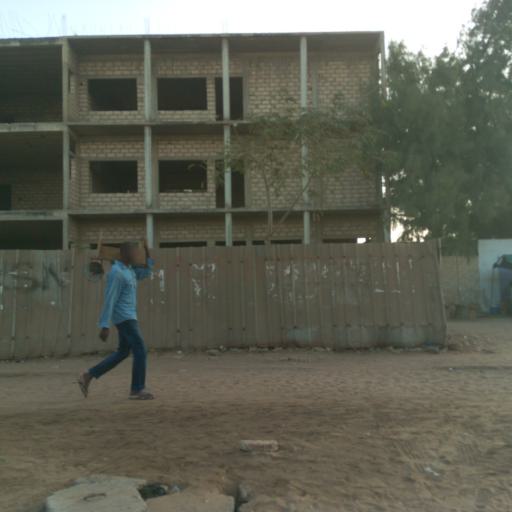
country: SN
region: Dakar
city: Dakar
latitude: 14.6984
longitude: -17.4525
